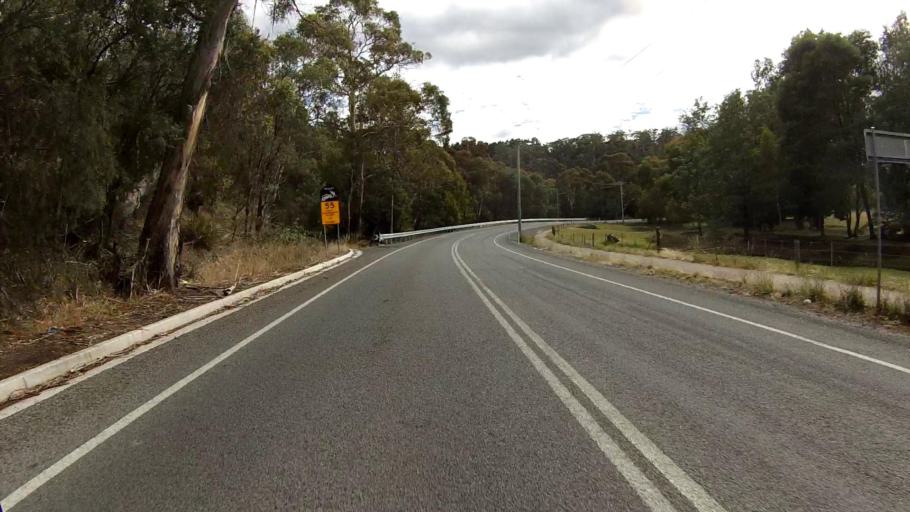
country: AU
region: Tasmania
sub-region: Glenorchy
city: Lutana
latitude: -42.8098
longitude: 147.3366
